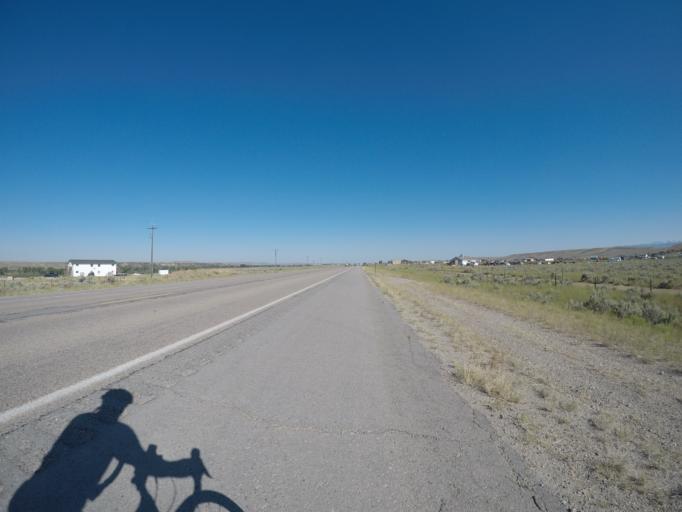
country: US
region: Wyoming
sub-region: Sublette County
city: Pinedale
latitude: 42.7631
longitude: -109.7372
